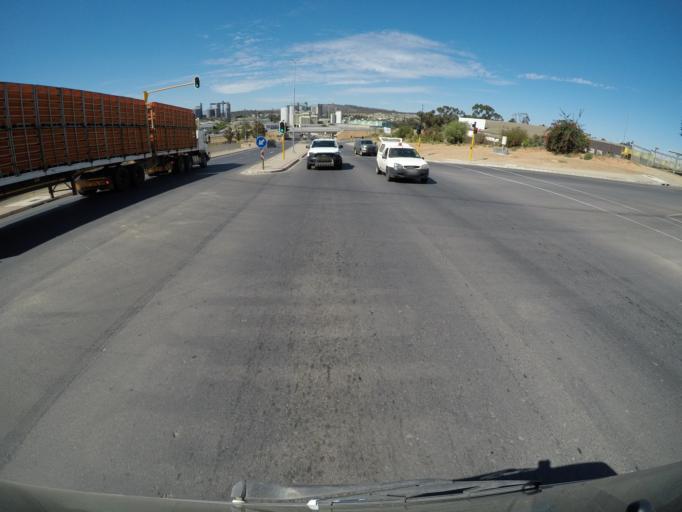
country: ZA
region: Western Cape
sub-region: West Coast District Municipality
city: Malmesbury
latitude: -33.4646
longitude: 18.7153
